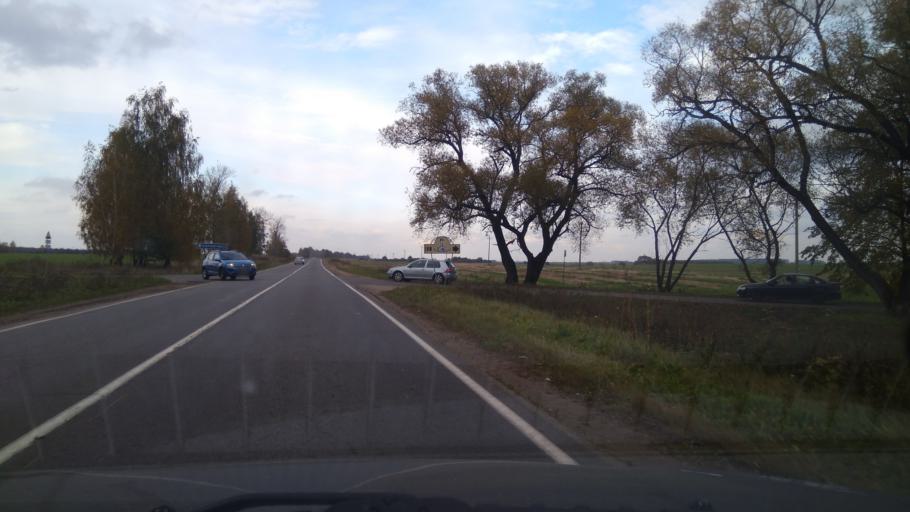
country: BY
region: Minsk
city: Dukora
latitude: 53.6811
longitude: 27.9565
